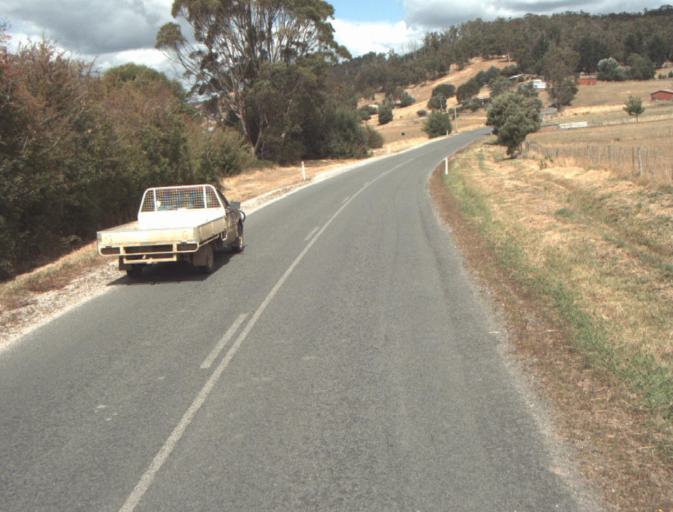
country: AU
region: Tasmania
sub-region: Launceston
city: Mayfield
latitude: -41.2309
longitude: 147.1245
